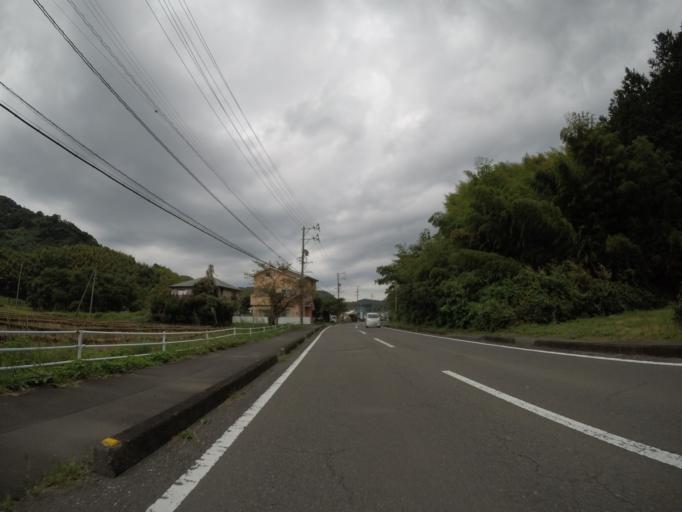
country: JP
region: Shizuoka
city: Fujieda
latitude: 34.9025
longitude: 138.2608
